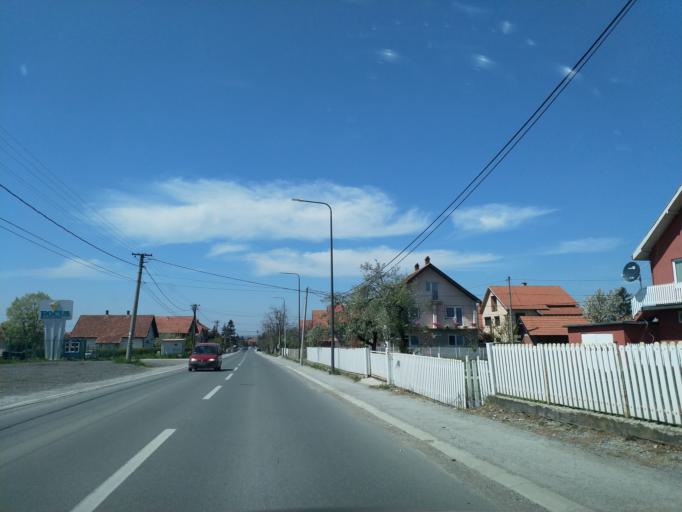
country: RS
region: Central Serbia
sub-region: Belgrade
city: Lazarevac
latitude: 44.3775
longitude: 20.2857
